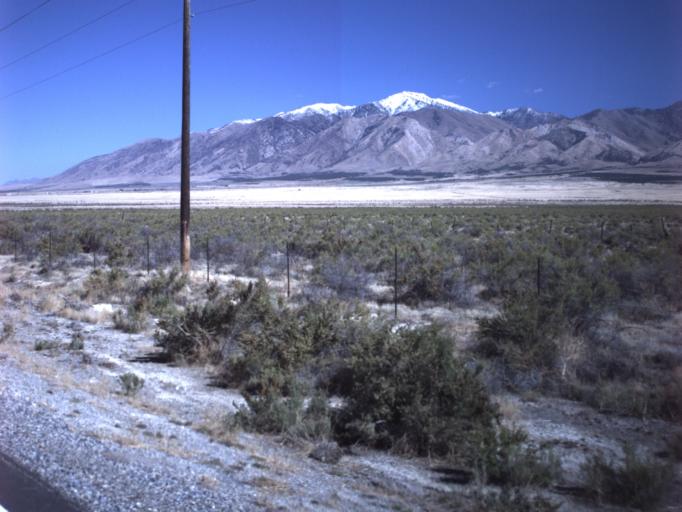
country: US
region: Utah
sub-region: Tooele County
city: Grantsville
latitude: 40.3497
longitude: -112.7453
